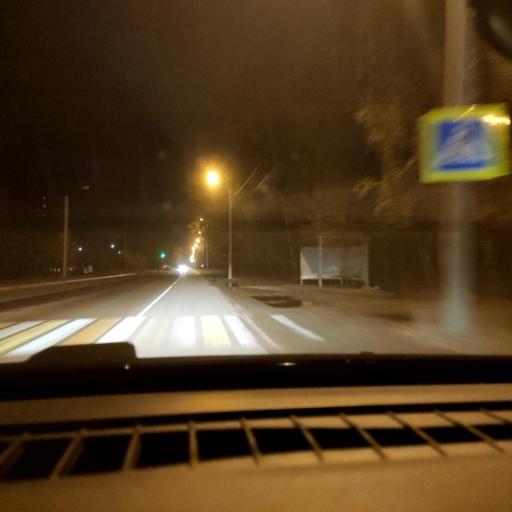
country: RU
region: Voronezj
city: Podgornoye
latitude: 51.7409
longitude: 39.1740
